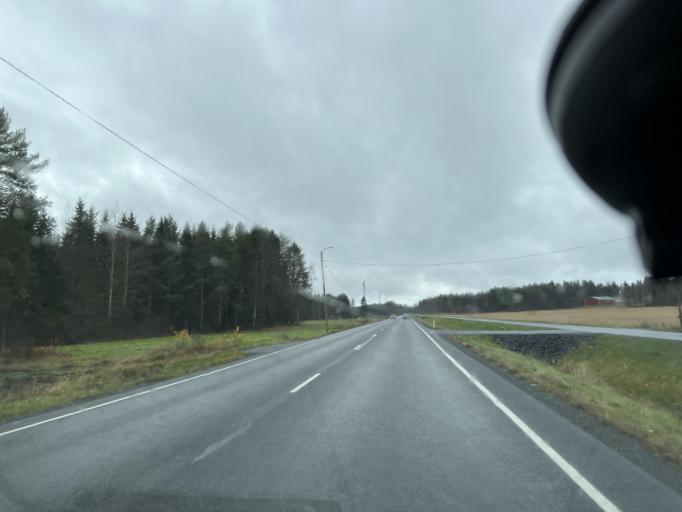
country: FI
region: Northern Ostrobothnia
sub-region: Ylivieska
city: Sievi
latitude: 63.9555
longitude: 24.5080
